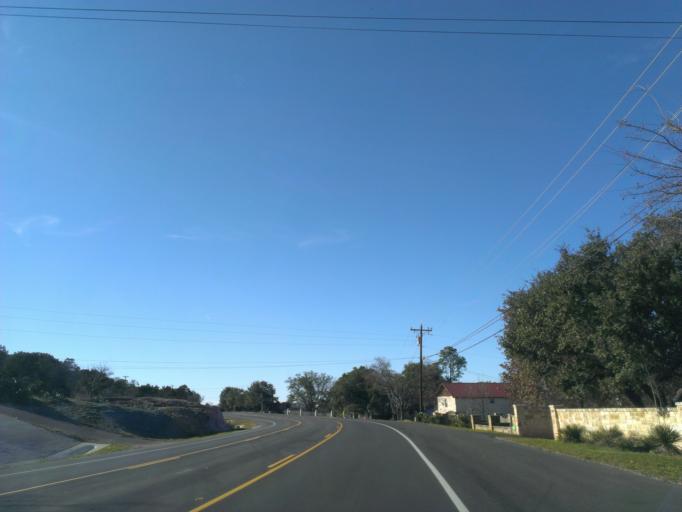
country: US
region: Texas
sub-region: Llano County
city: Horseshoe Bay
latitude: 30.5488
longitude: -98.3392
